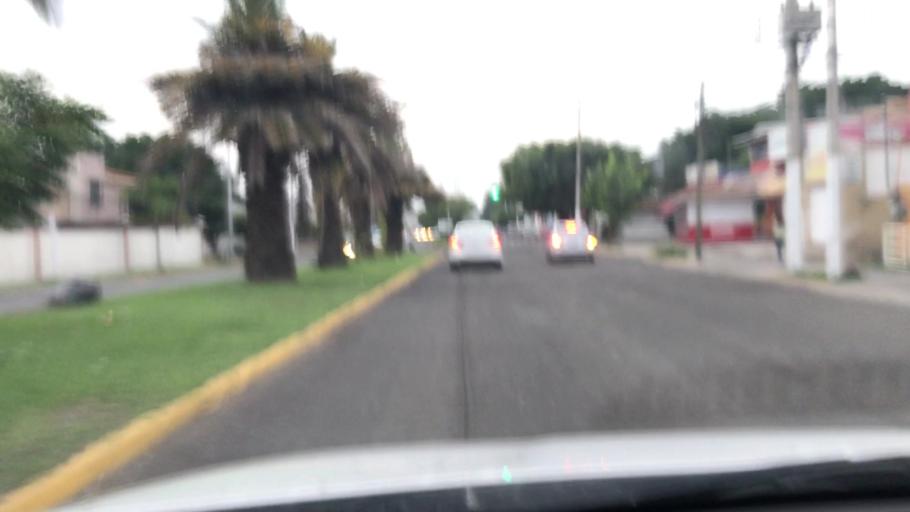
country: MX
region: Jalisco
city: Guadalajara
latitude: 20.6509
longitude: -103.4262
